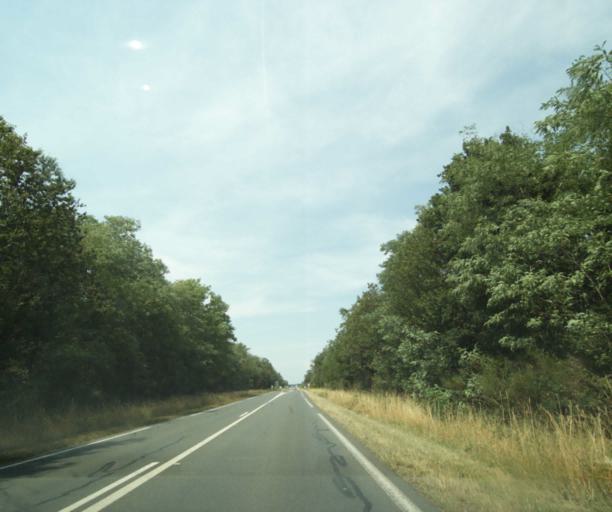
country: FR
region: Poitou-Charentes
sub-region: Departement de la Vienne
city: Cenon-sur-Vienne
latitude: 46.7700
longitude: 0.5508
